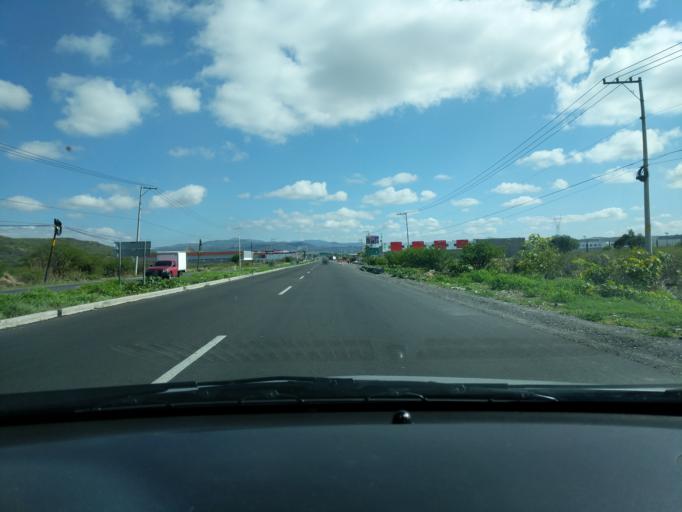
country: MX
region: Queretaro
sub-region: Queretaro
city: Patria Nueva
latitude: 20.6344
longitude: -100.4995
